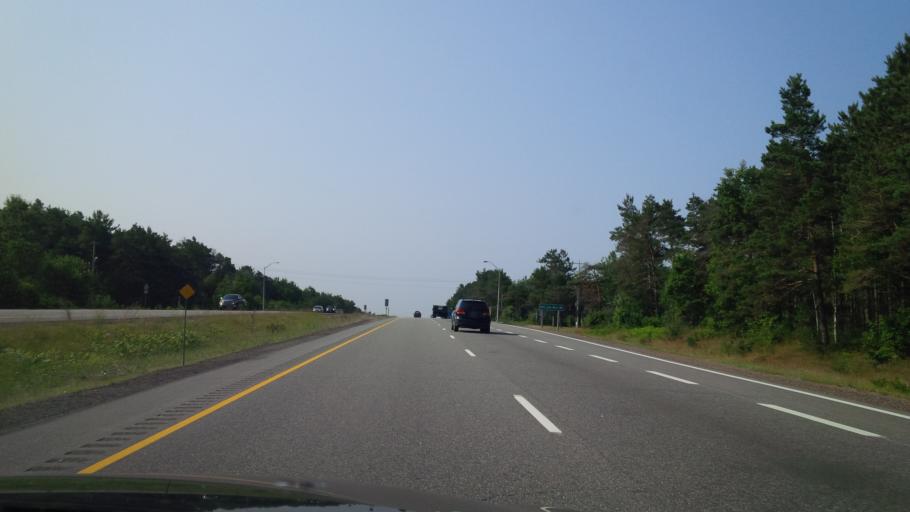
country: CA
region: Ontario
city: Bracebridge
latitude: 45.0743
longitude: -79.2970
